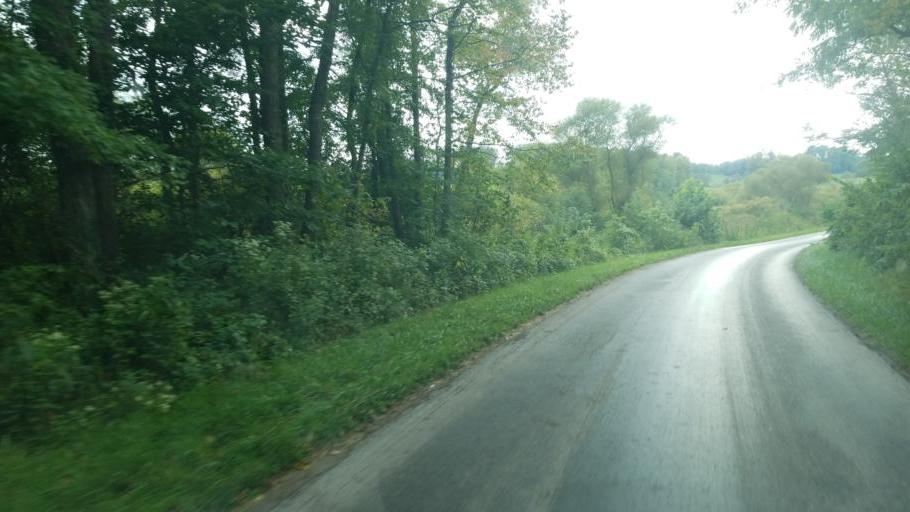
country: US
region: Ohio
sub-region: Jackson County
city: Oak Hill
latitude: 38.9266
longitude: -82.6103
